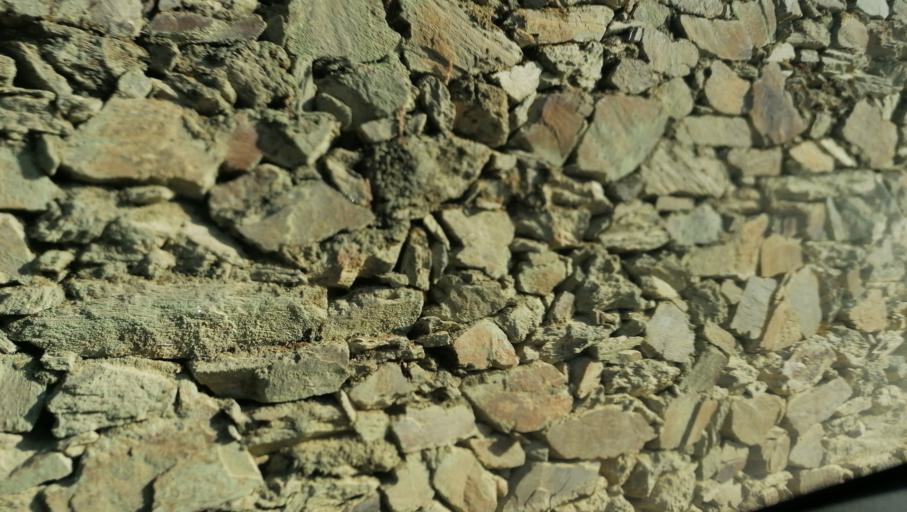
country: PT
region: Viseu
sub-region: Tabuaco
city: Tabuaco
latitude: 41.1498
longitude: -7.5936
